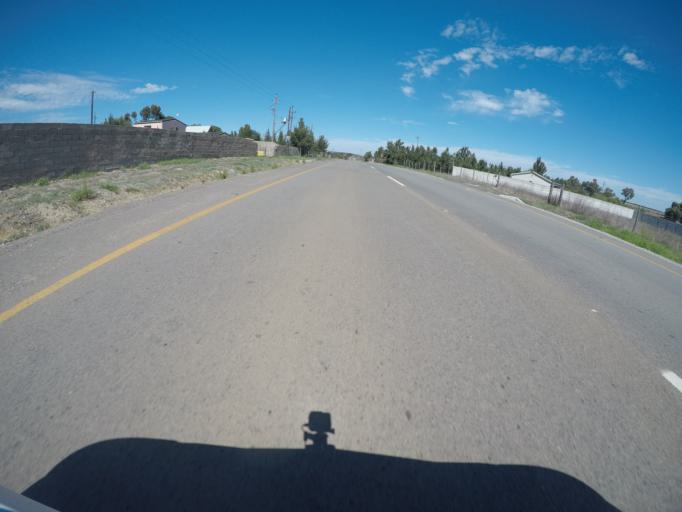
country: ZA
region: Western Cape
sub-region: West Coast District Municipality
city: Malmesbury
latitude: -33.5778
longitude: 18.6469
